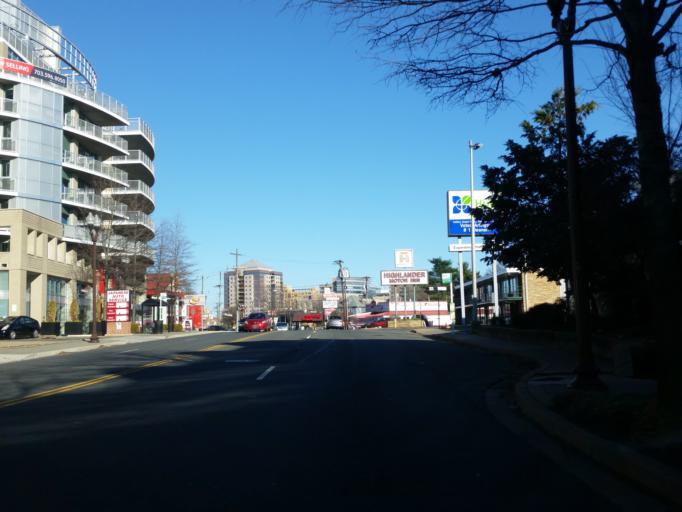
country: US
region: Virginia
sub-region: Arlington County
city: Arlington
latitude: 38.8828
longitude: -77.1008
